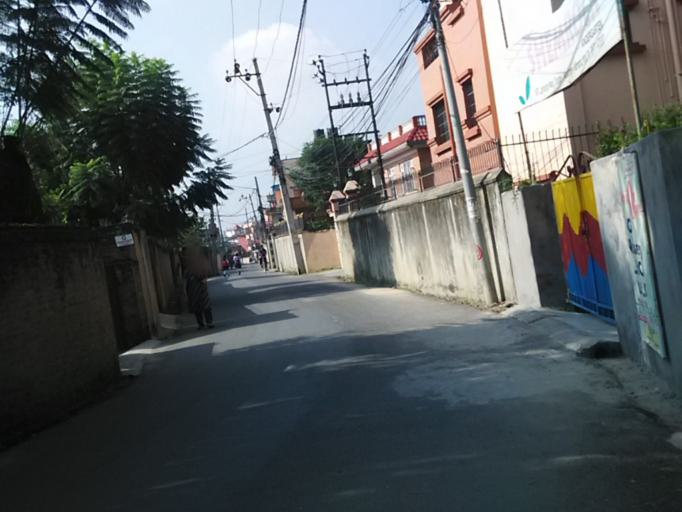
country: NP
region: Central Region
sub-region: Bagmati Zone
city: Kathmandu
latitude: 27.7343
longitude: 85.3368
